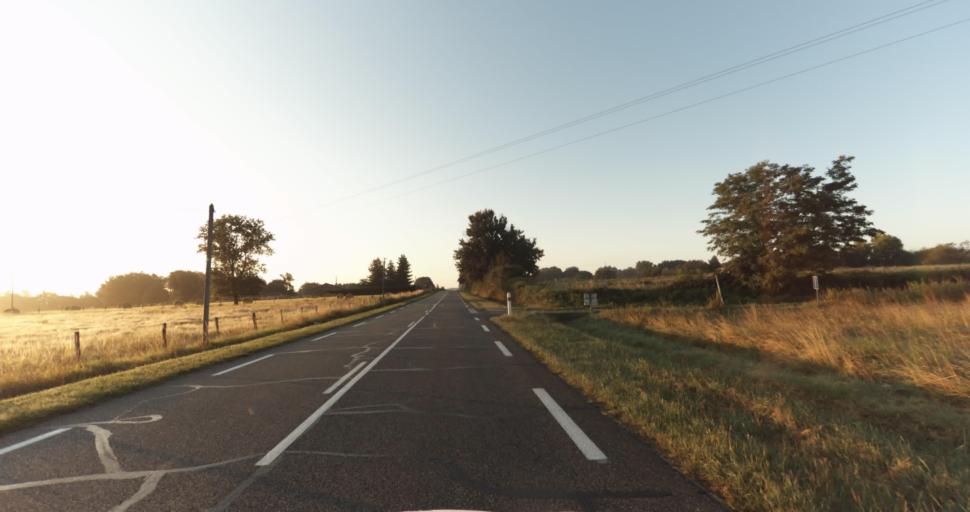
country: FR
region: Aquitaine
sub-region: Departement de la Gironde
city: Bazas
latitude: 44.4276
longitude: -0.1901
